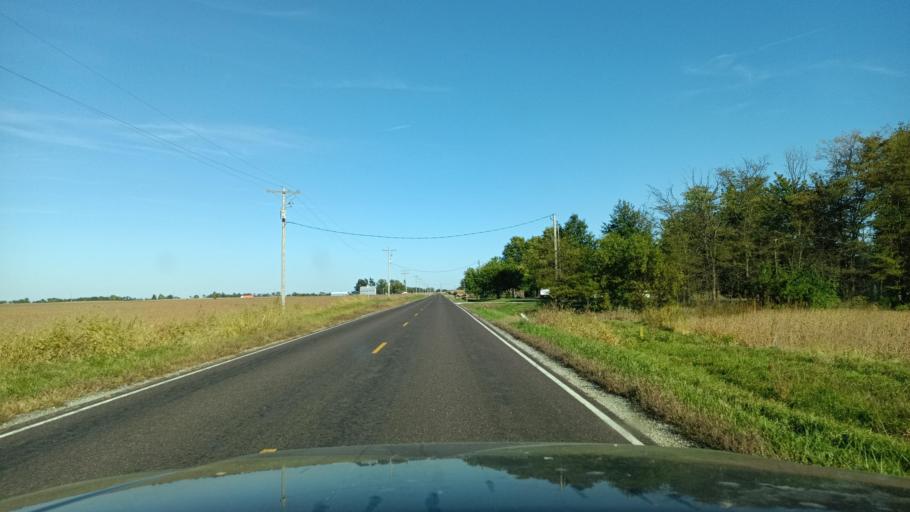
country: US
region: Illinois
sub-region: De Witt County
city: Clinton
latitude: 40.2315
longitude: -88.9872
